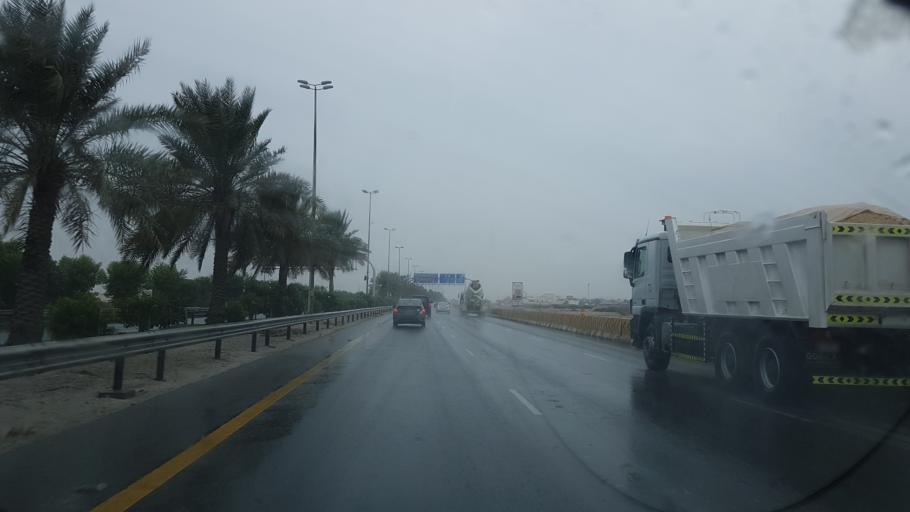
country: BH
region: Manama
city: Jidd Hafs
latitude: 26.2062
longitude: 50.5154
